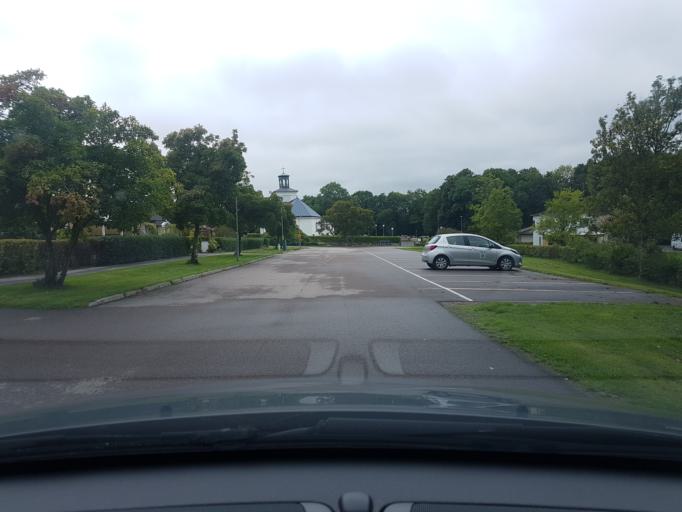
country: SE
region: Vaestra Goetaland
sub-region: Ale Kommun
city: Nodinge-Nol
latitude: 57.8904
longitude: 12.0620
